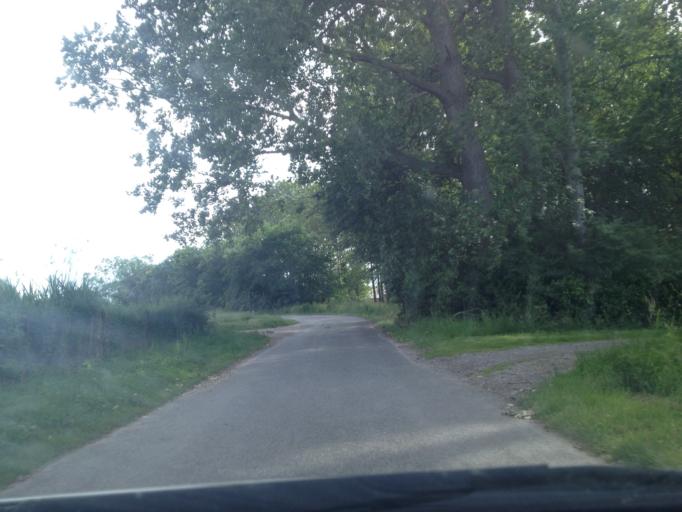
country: DK
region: Central Jutland
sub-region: Samso Kommune
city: Tranebjerg
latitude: 55.7825
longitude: 10.5528
